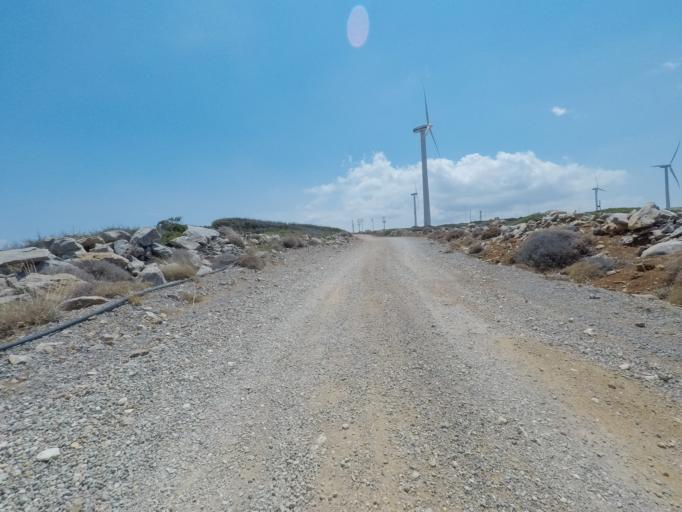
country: GR
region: Crete
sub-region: Nomos Lasithiou
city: Elounda
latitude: 35.3267
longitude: 25.7559
